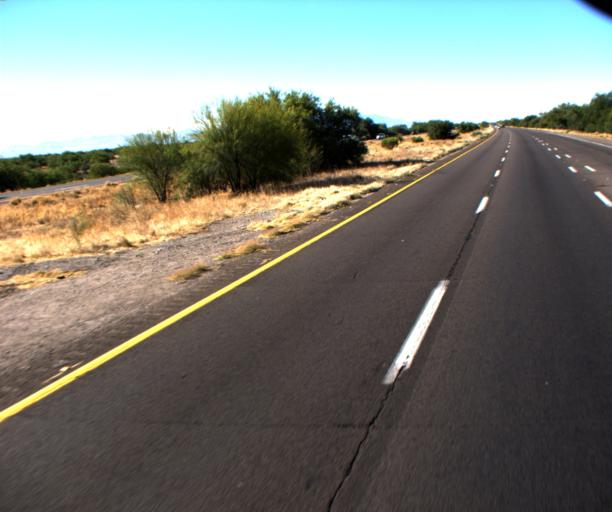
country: US
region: Arizona
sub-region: Pima County
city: Drexel Heights
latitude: 32.1016
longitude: -110.9935
